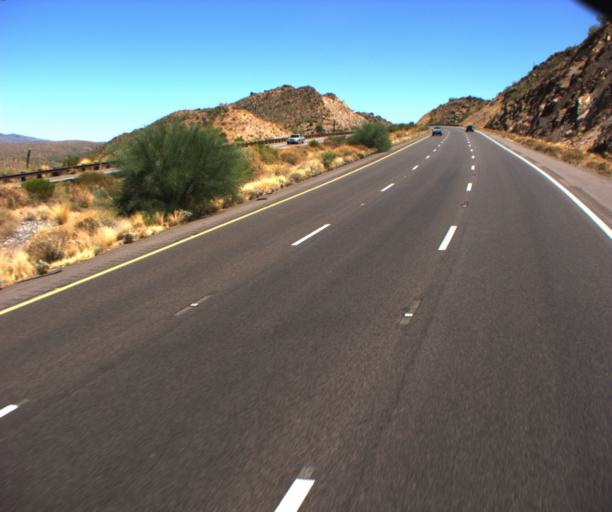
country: US
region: Arizona
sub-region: Maricopa County
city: Rio Verde
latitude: 33.7051
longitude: -111.5059
